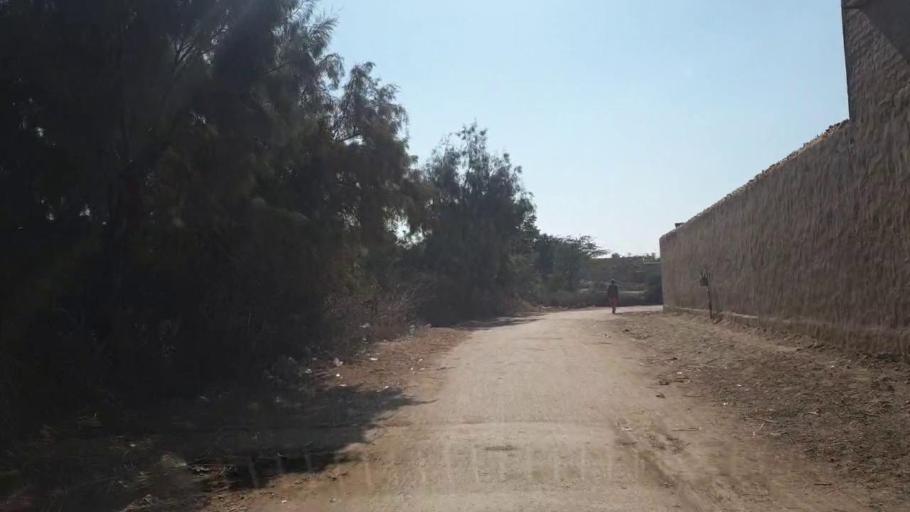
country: PK
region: Sindh
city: Shahpur Chakar
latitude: 26.1059
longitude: 68.6358
